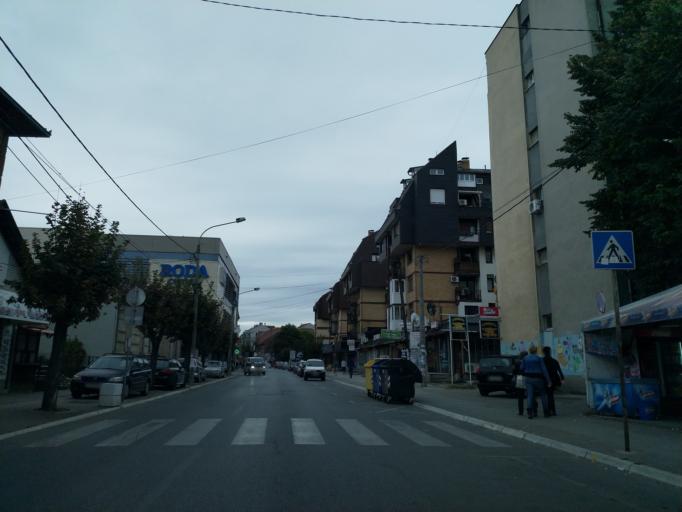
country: RS
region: Central Serbia
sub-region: Pomoravski Okrug
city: Jagodina
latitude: 43.9822
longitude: 21.2547
